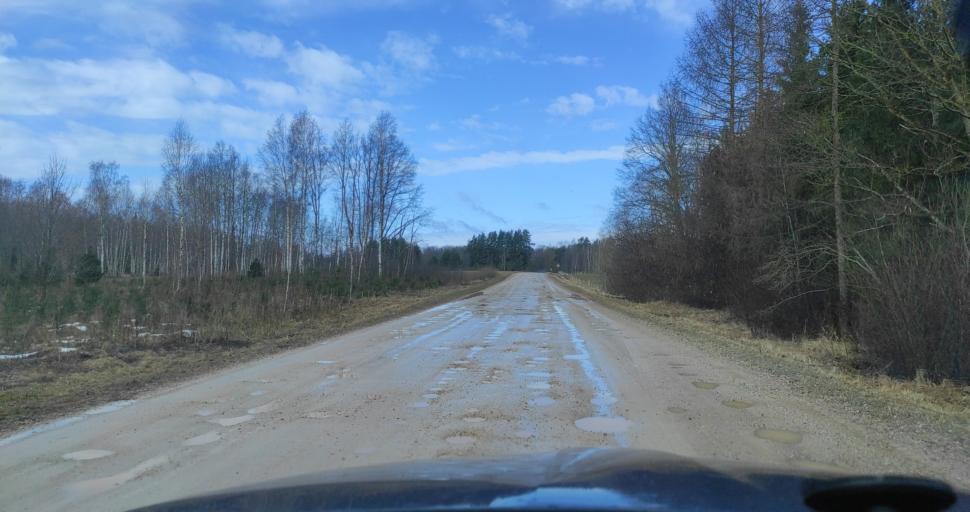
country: LV
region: Tukuma Rajons
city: Tukums
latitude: 57.1084
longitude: 23.0351
